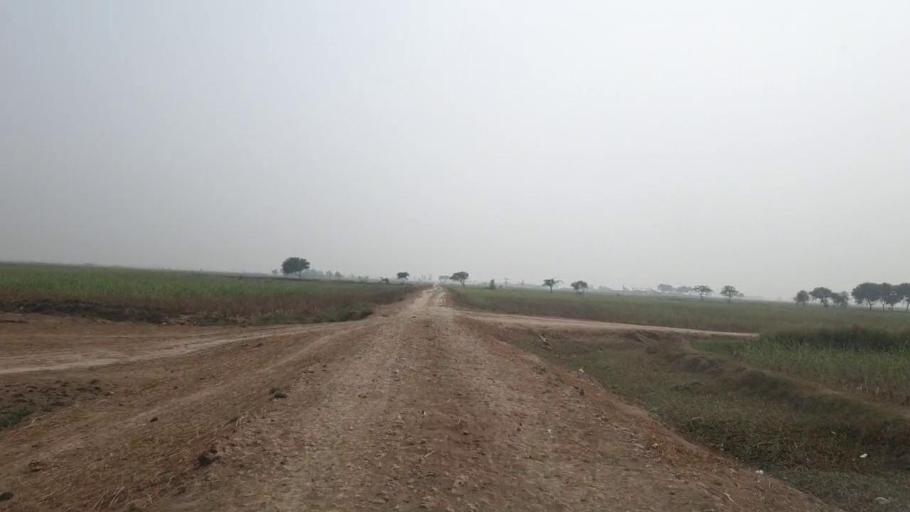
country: PK
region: Sindh
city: Kario
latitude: 24.6294
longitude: 68.5958
